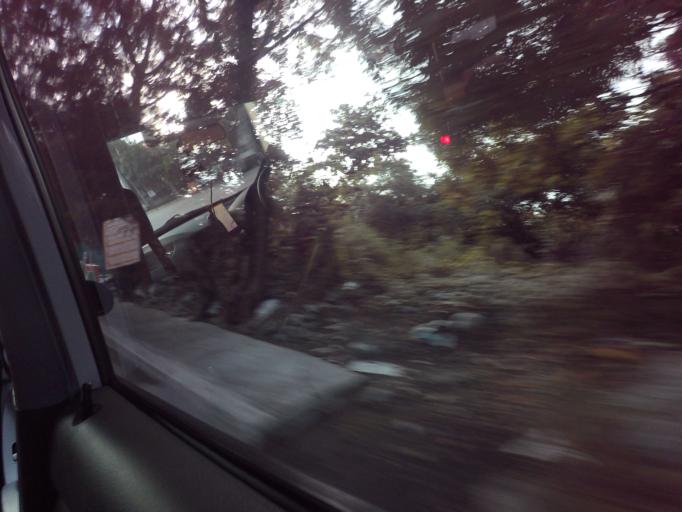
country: PH
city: Sambayanihan People's Village
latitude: 14.4701
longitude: 120.9868
